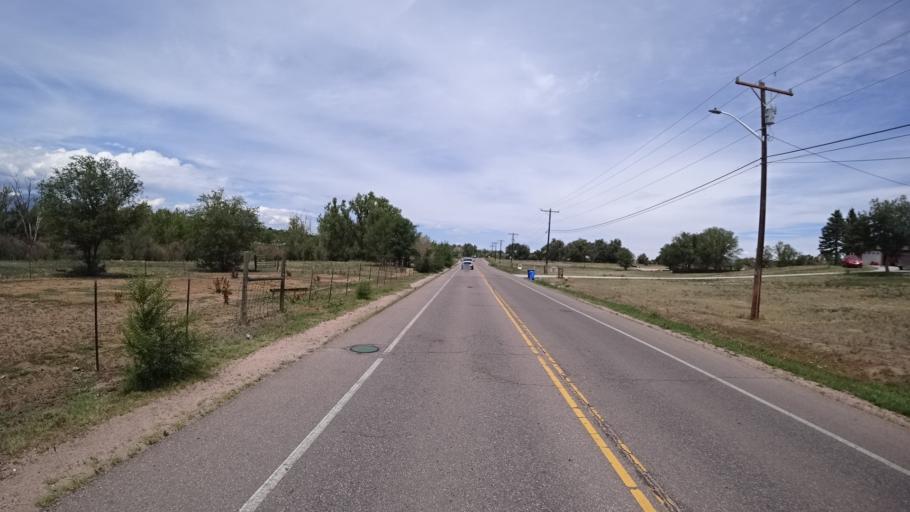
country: US
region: Colorado
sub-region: El Paso County
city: Fountain
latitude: 38.6816
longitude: -104.6876
